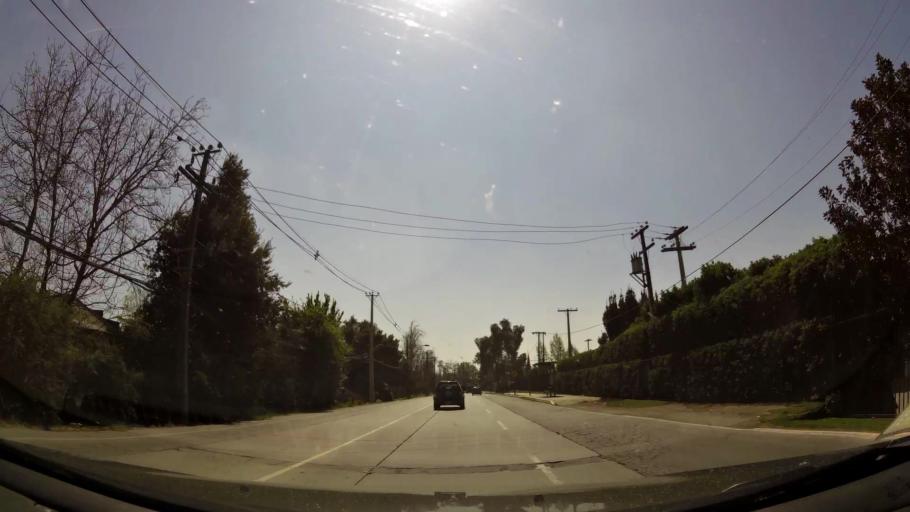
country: CL
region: Santiago Metropolitan
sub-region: Provincia de Santiago
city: Lo Prado
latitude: -33.3673
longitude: -70.7056
